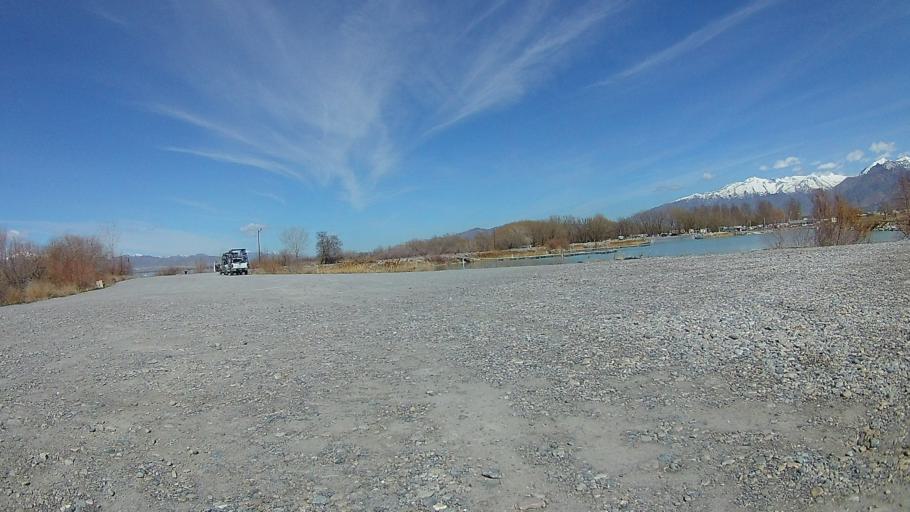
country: US
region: Utah
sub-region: Utah County
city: American Fork
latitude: 40.3401
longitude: -111.8013
